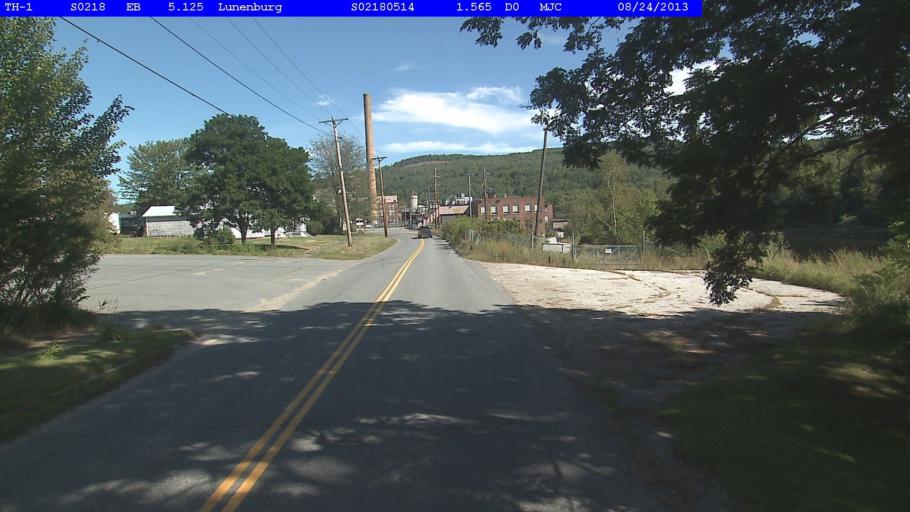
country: US
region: New Hampshire
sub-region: Grafton County
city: Littleton
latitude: 44.4118
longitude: -71.7214
